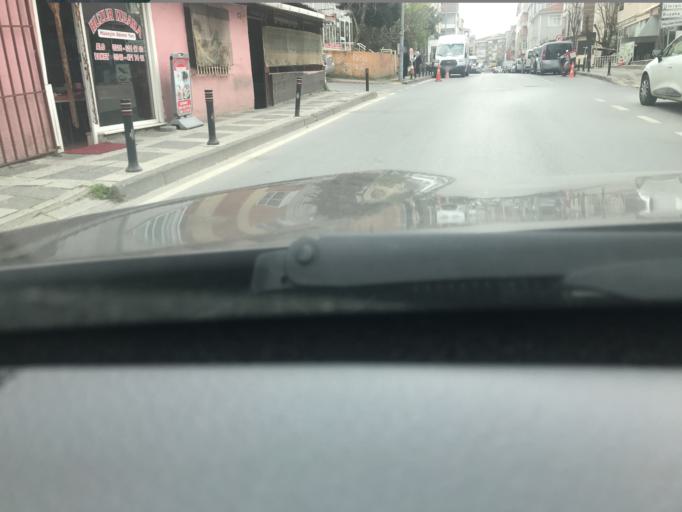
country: TR
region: Istanbul
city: Umraniye
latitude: 41.0239
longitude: 29.1325
